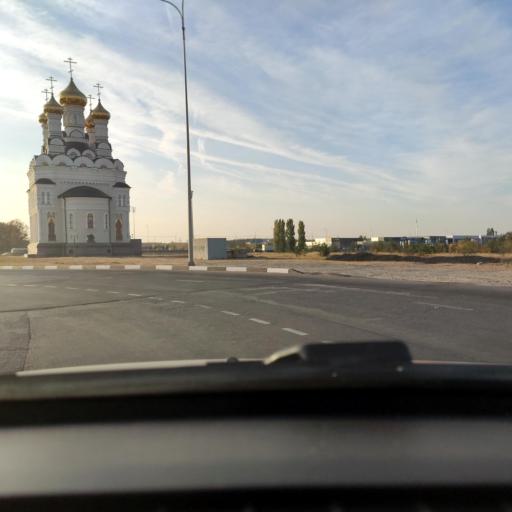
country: RU
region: Voronezj
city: Podgornoye
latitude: 51.7916
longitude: 39.2033
